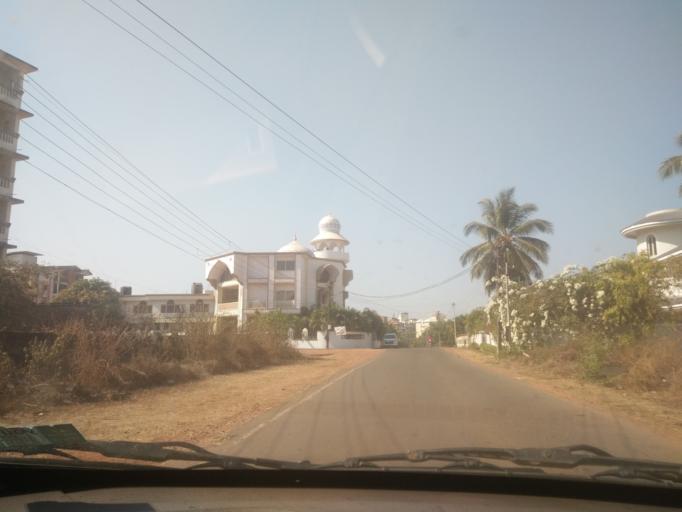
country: IN
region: Goa
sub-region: South Goa
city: Chicalim
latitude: 15.3917
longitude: 73.8606
